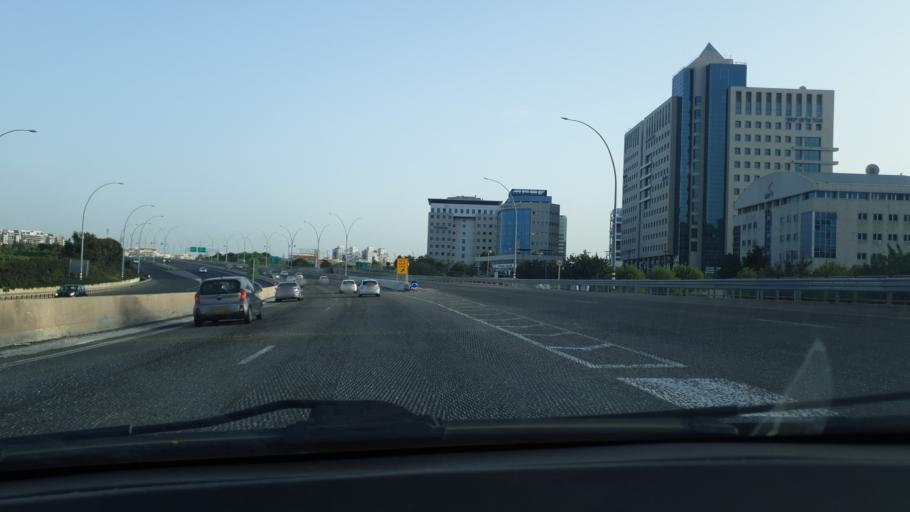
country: IL
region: Central District
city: Ra'anana
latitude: 32.1985
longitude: 34.8848
